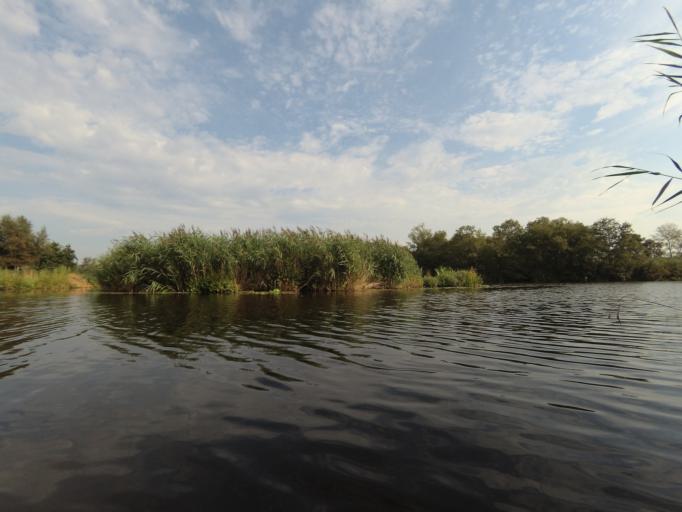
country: NL
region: South Holland
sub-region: Gemeente Nieuwkoop
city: Nieuwkoop
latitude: 52.1610
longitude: 4.8230
